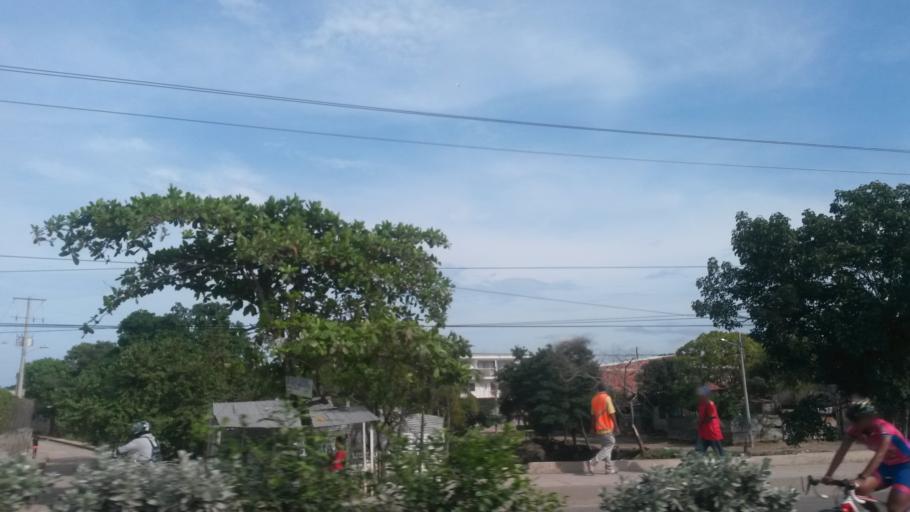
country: CO
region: Bolivar
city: Cartagena
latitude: 10.4036
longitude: -75.4577
